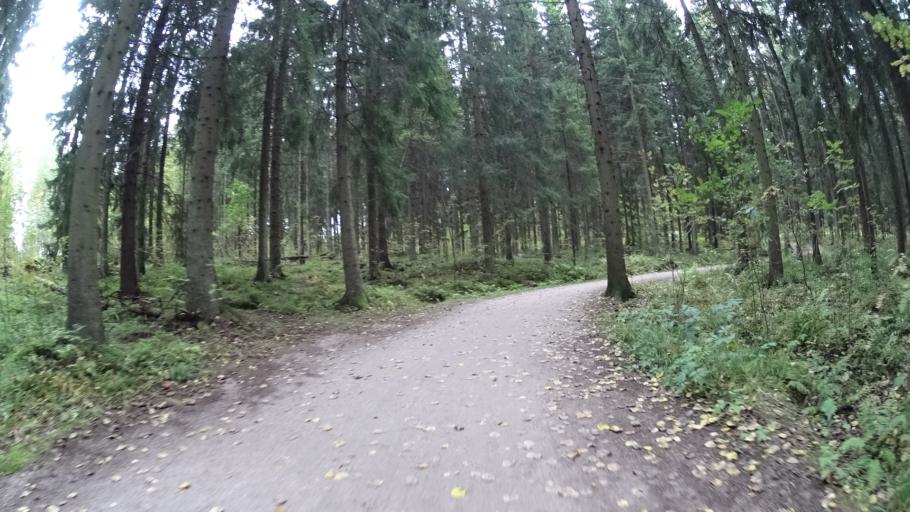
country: FI
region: Uusimaa
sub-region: Helsinki
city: Helsinki
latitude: 60.2493
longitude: 24.9150
